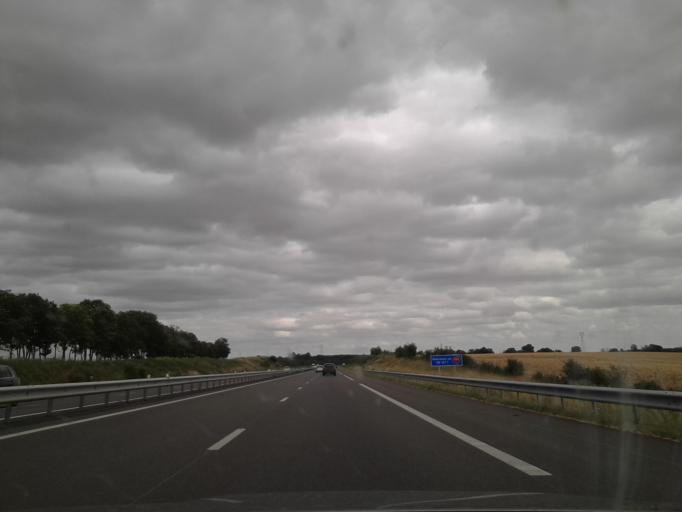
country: FR
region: Centre
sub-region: Departement du Cher
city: Trouy
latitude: 47.0391
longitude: 2.3549
